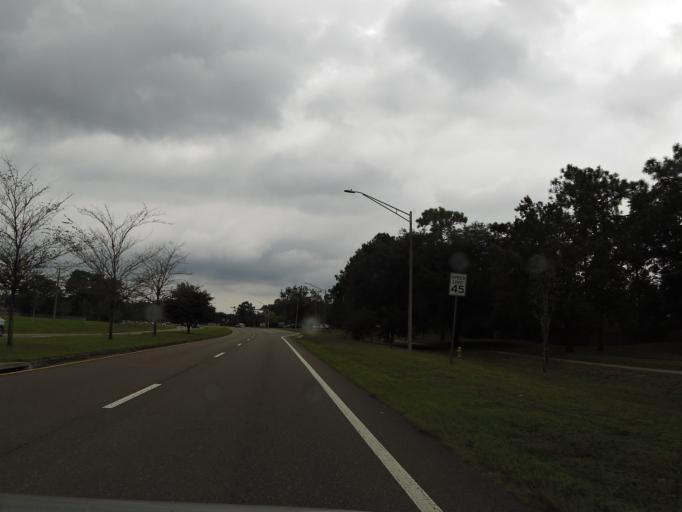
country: US
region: Florida
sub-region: Clay County
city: Bellair-Meadowbrook Terrace
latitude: 30.1967
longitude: -81.7962
